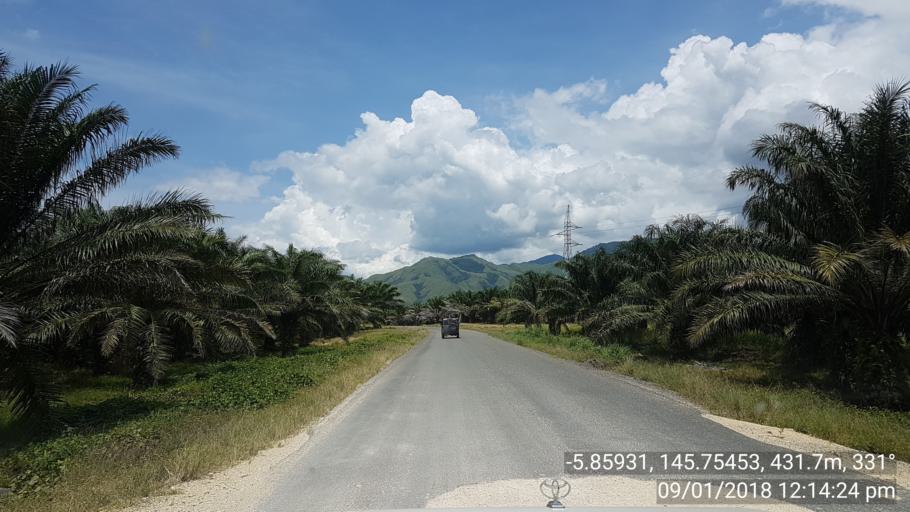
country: PG
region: Eastern Highlands
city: Goroka
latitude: -5.8595
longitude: 145.7547
